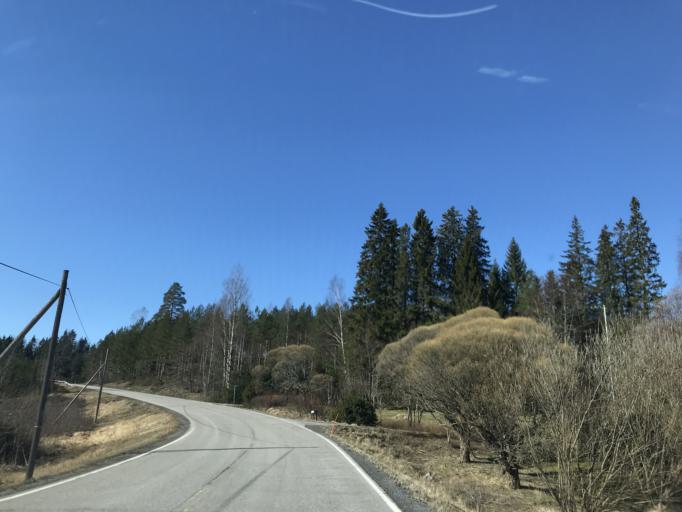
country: FI
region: Uusimaa
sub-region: Raaseporin
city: Pohja
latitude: 60.0902
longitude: 23.4444
